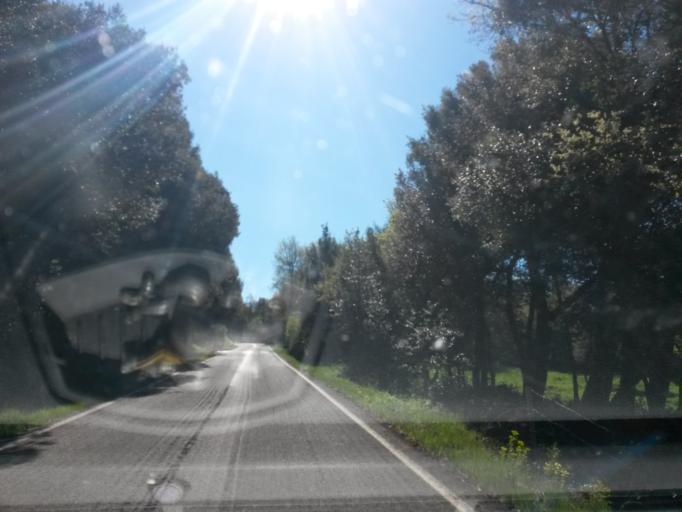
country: ES
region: Catalonia
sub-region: Provincia de Girona
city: Sant Cristofol de les Fonts
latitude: 42.1753
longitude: 2.5142
